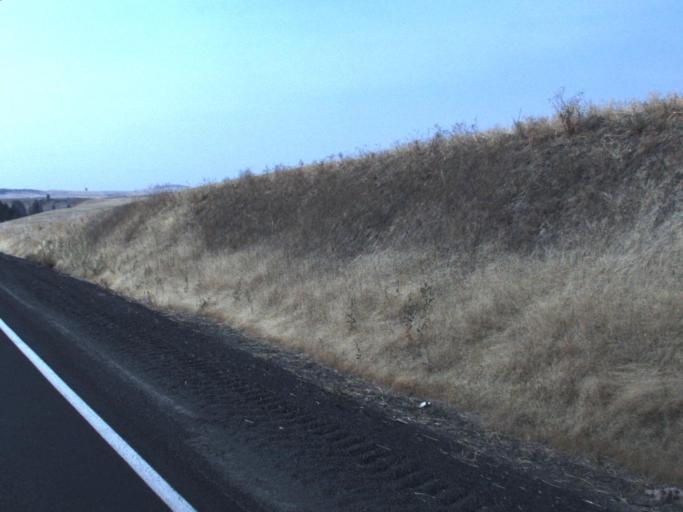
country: US
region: Washington
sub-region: Whitman County
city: Pullman
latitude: 46.9496
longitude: -117.0919
